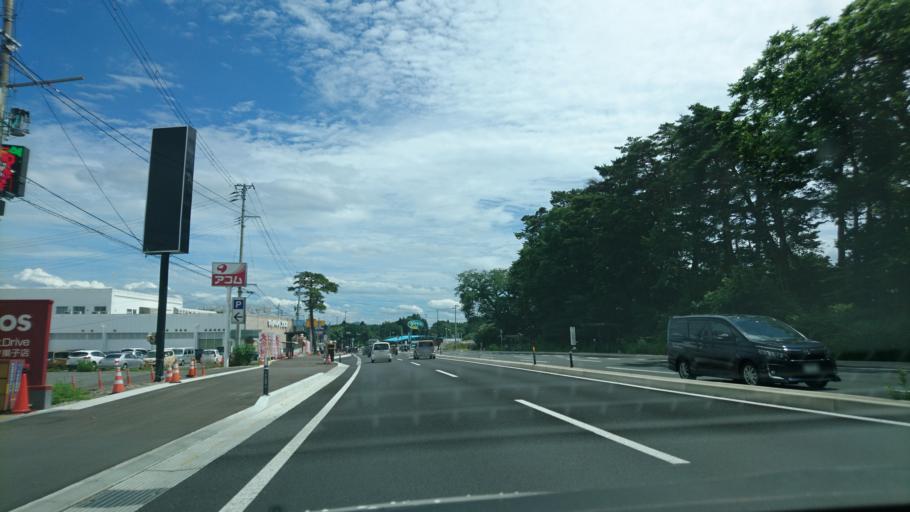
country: JP
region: Iwate
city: Morioka-shi
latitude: 39.7736
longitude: 141.1281
